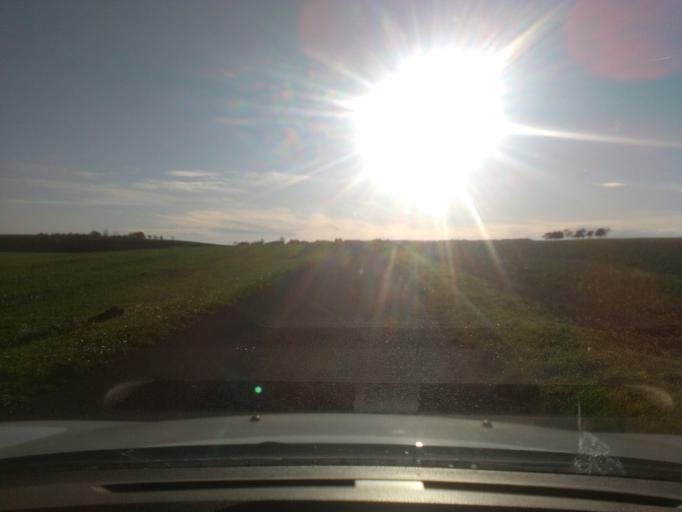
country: FR
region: Lorraine
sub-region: Departement des Vosges
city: Rambervillers
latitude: 48.2855
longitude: 6.5867
